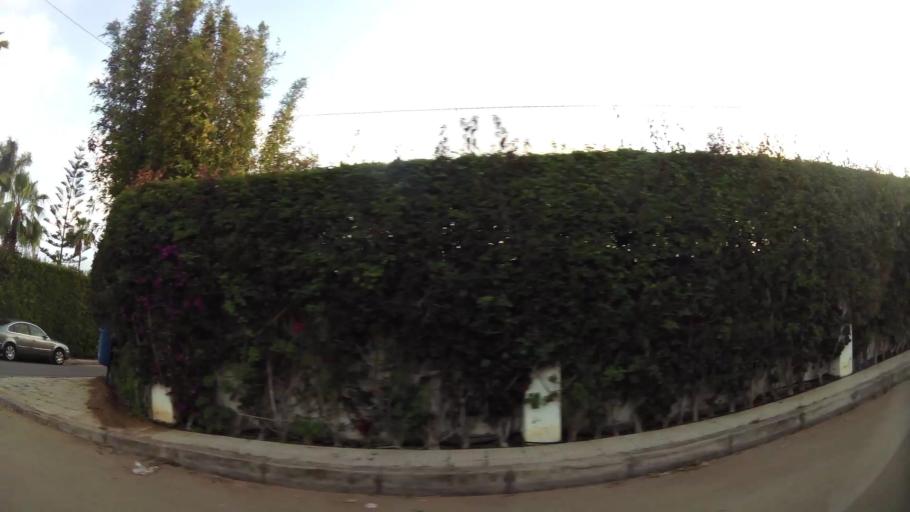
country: MA
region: Rabat-Sale-Zemmour-Zaer
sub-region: Rabat
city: Rabat
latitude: 33.9706
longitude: -6.8370
